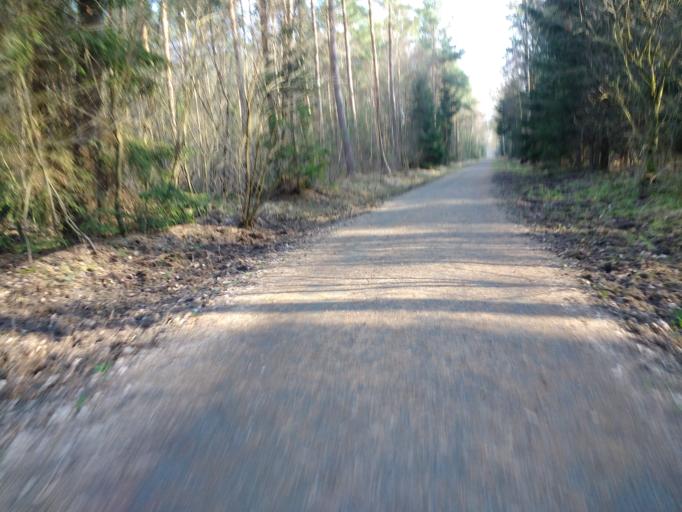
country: DE
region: Lower Saxony
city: Gifhorn
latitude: 52.4609
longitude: 10.5650
